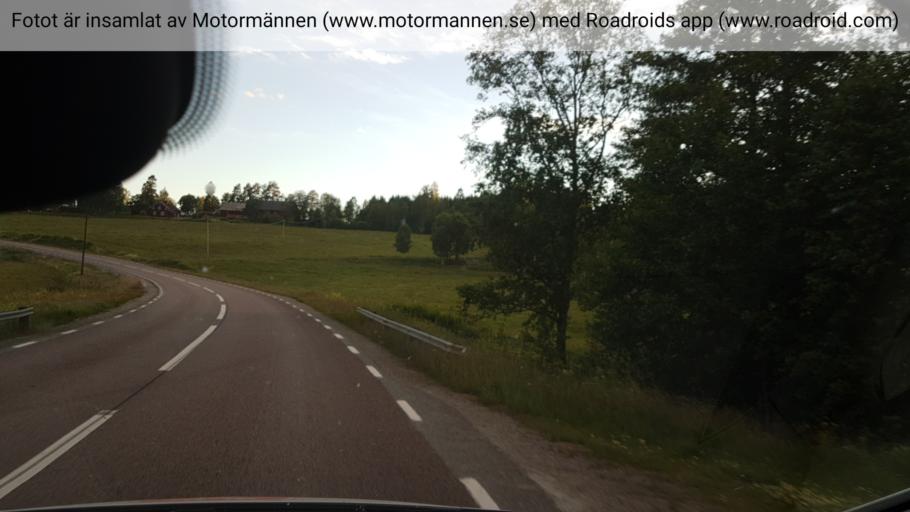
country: SE
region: Vaermland
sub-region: Sunne Kommun
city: Sunne
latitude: 59.6680
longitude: 13.0106
